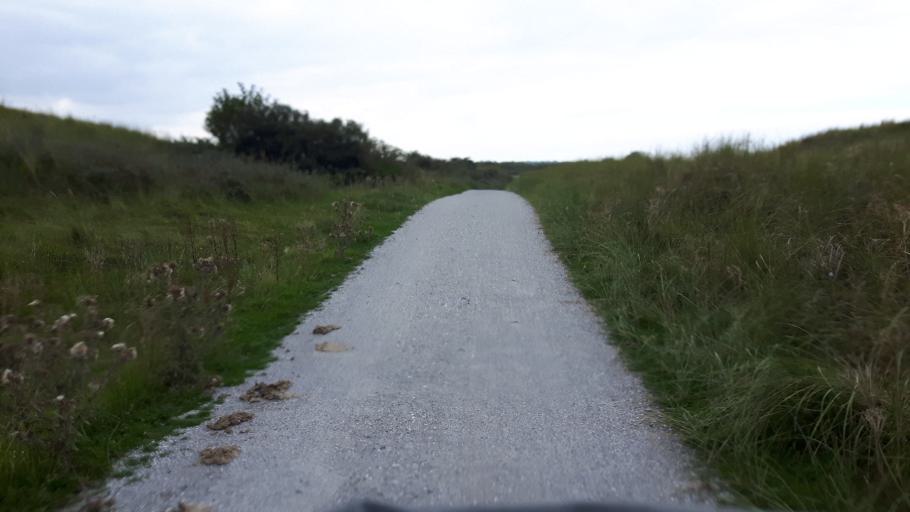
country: NL
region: Friesland
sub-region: Gemeente Ameland
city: Nes
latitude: 53.4570
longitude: 5.8288
